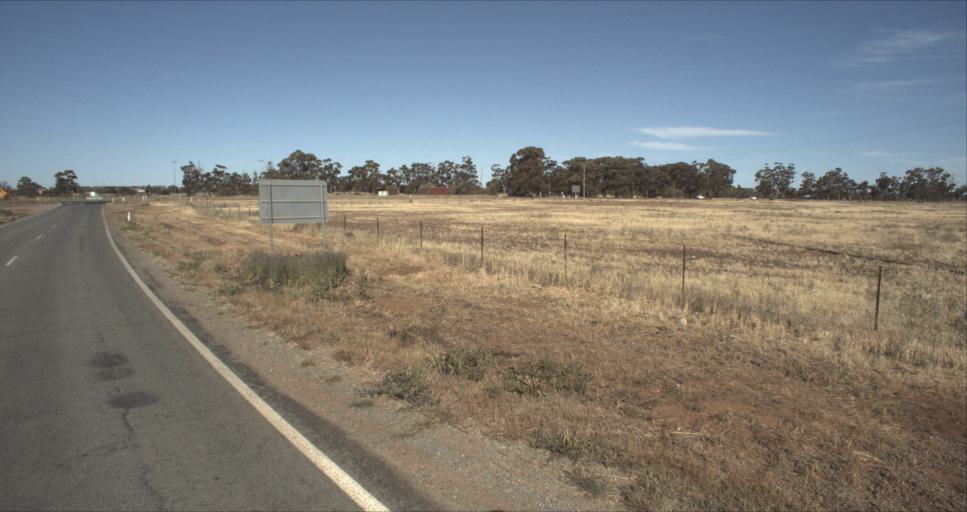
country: AU
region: New South Wales
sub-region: Leeton
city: Leeton
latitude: -34.6086
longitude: 146.4067
